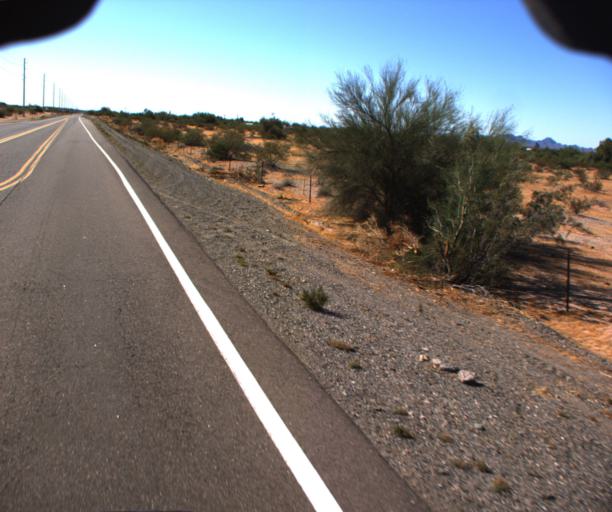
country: US
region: Arizona
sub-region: La Paz County
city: Cienega Springs
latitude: 33.9607
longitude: -114.0317
